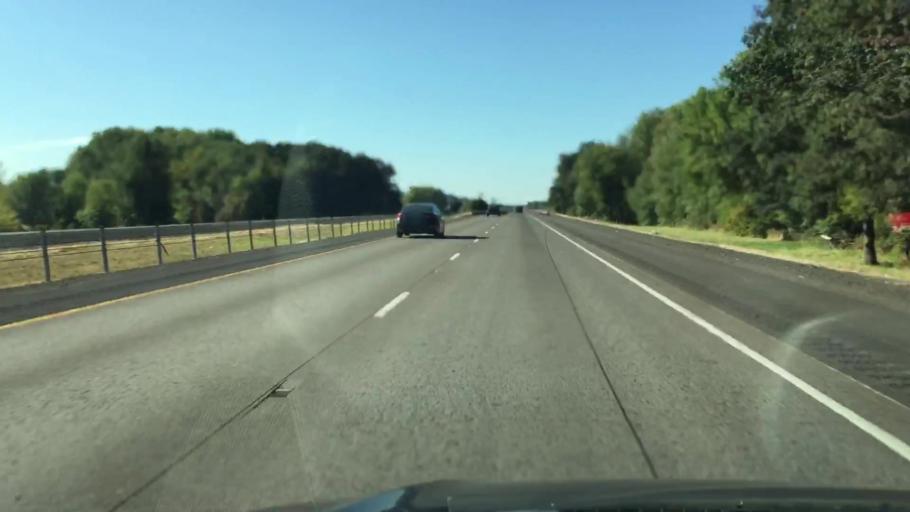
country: US
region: Oregon
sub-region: Linn County
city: Tangent
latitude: 44.4762
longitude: -123.0618
